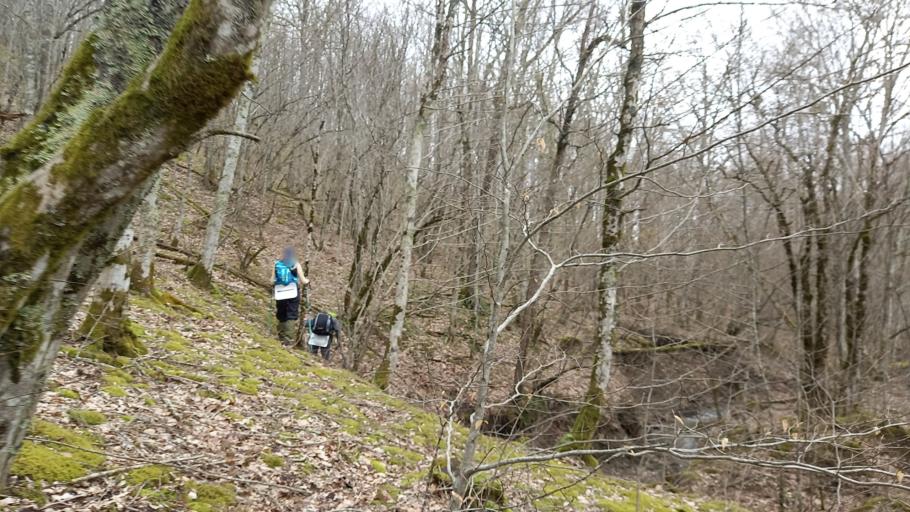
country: RU
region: Krasnodarskiy
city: Pshada
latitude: 44.4949
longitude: 38.3855
